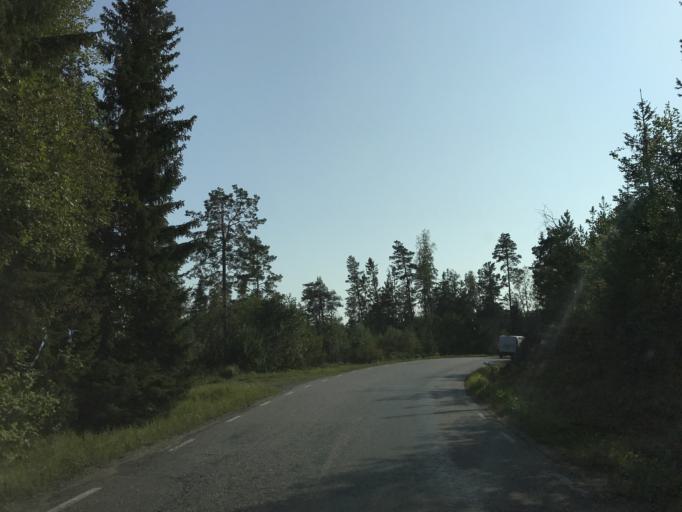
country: SE
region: Stockholm
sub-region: Norrtalje Kommun
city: Bjorko
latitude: 59.8651
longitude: 19.0469
